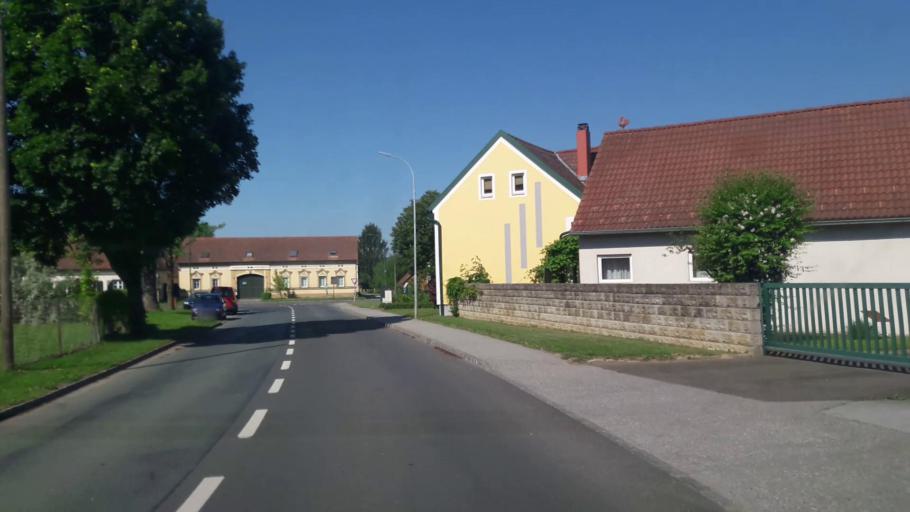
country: AT
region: Burgenland
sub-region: Politischer Bezirk Jennersdorf
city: Deutsch Kaltenbrunn
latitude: 47.0911
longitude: 16.1061
